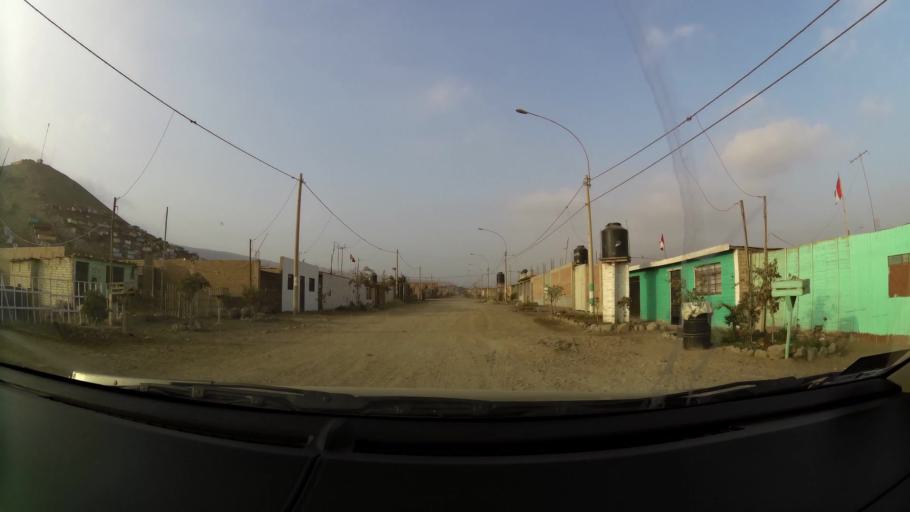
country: PE
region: Lima
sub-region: Lima
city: Santa Rosa
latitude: -11.7450
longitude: -77.1480
